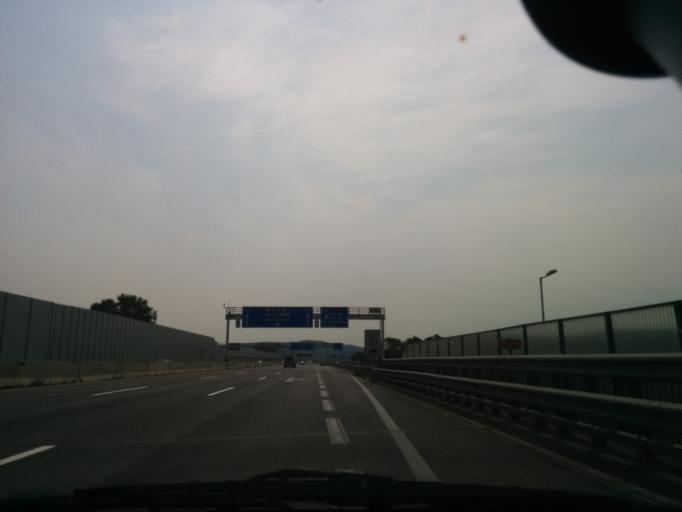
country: AT
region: Lower Austria
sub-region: Politischer Bezirk Korneuburg
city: Leobendorf
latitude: 48.3597
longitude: 16.3078
